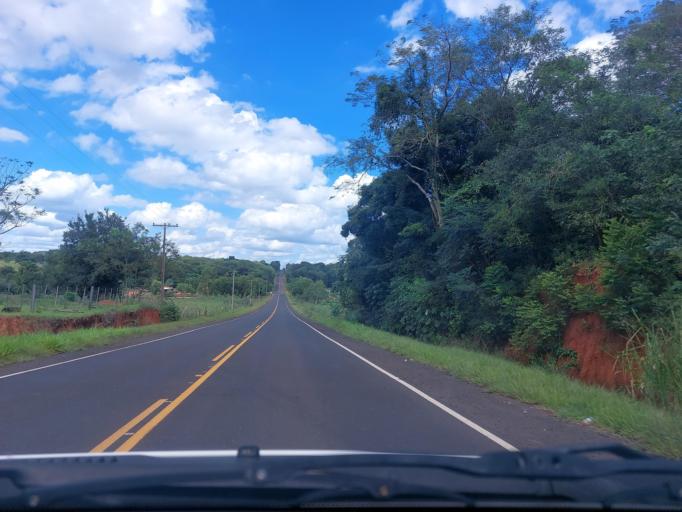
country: PY
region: San Pedro
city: Guayaybi
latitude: -24.5466
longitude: -56.5196
